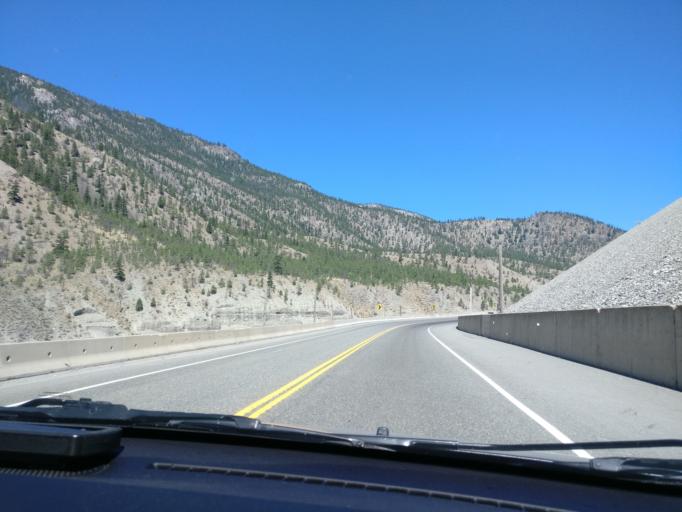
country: CA
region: British Columbia
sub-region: Thompson-Nicola Regional District
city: Ashcroft
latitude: 50.2789
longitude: -121.4060
